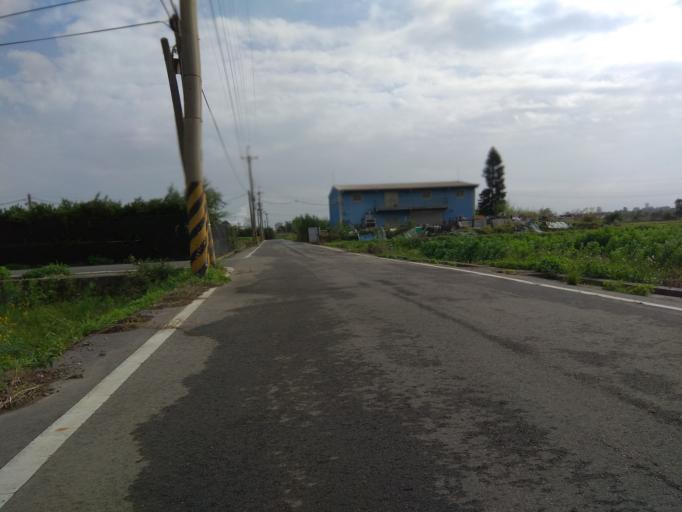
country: TW
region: Taiwan
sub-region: Hsinchu
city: Zhubei
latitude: 24.9784
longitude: 121.0323
